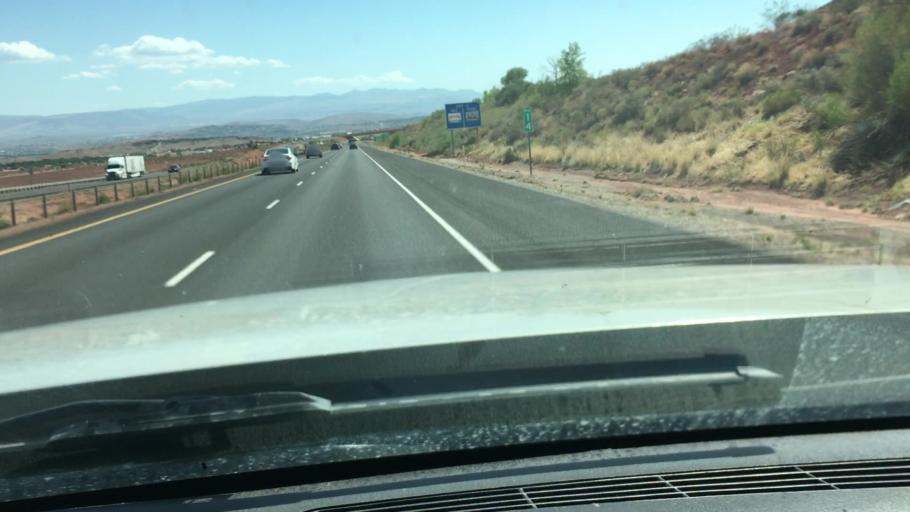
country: US
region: Utah
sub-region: Washington County
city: Washington
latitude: 37.1539
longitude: -113.4804
